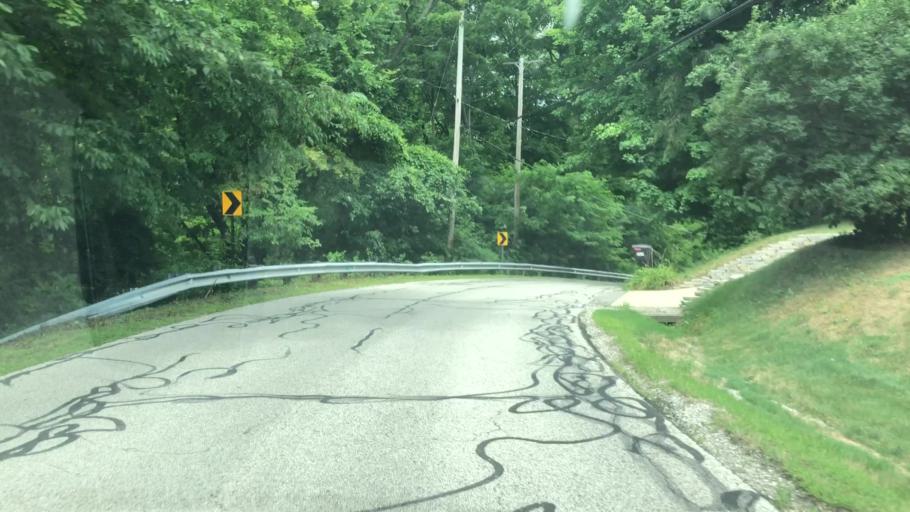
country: US
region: Ohio
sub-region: Summit County
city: Montrose-Ghent
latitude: 41.1552
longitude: -81.6382
